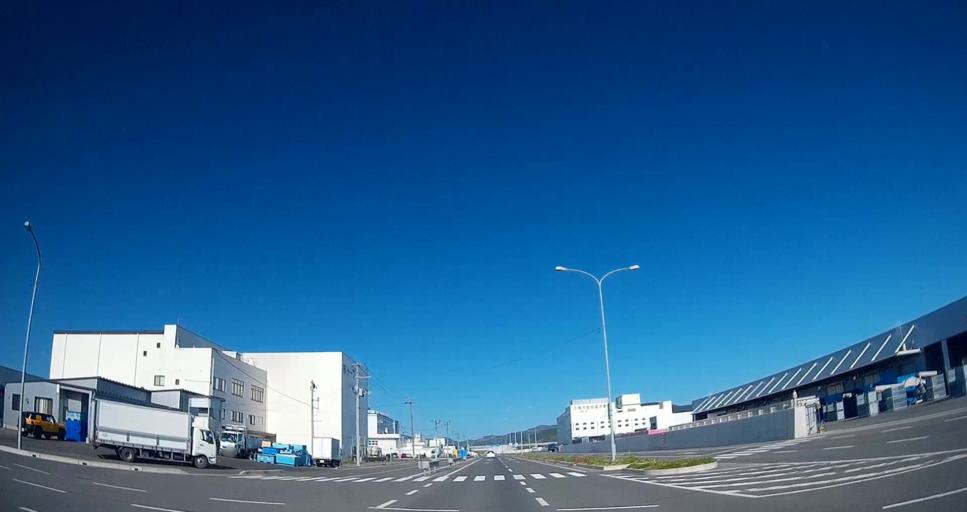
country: JP
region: Miyagi
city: Ishinomaki
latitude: 38.4132
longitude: 141.3355
